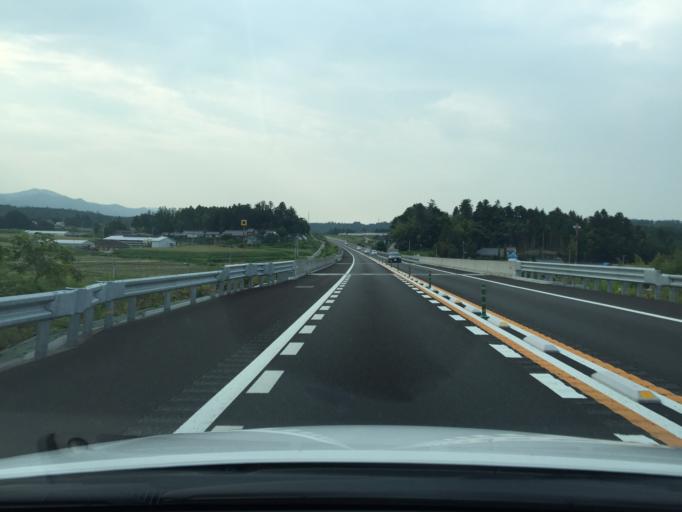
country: JP
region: Fukushima
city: Namie
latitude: 37.5721
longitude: 140.9428
